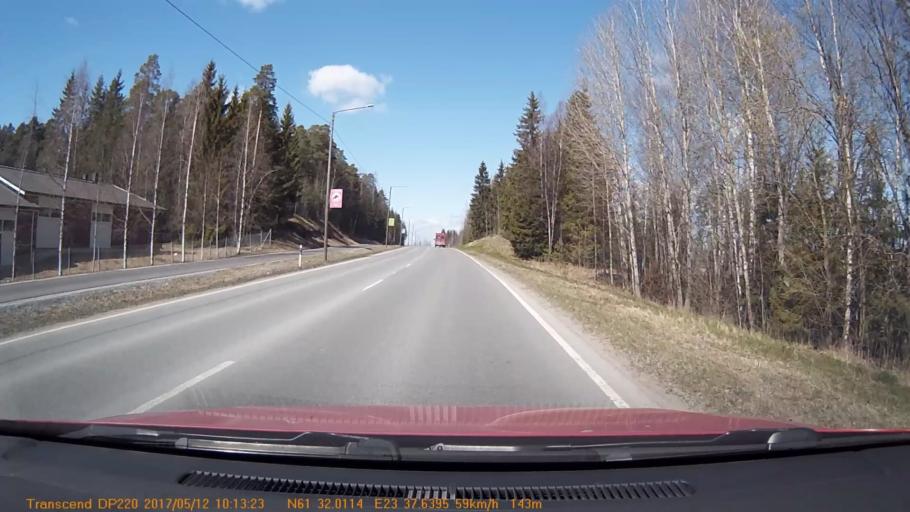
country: FI
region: Pirkanmaa
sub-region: Tampere
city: Yloejaervi
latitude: 61.5335
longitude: 23.6273
